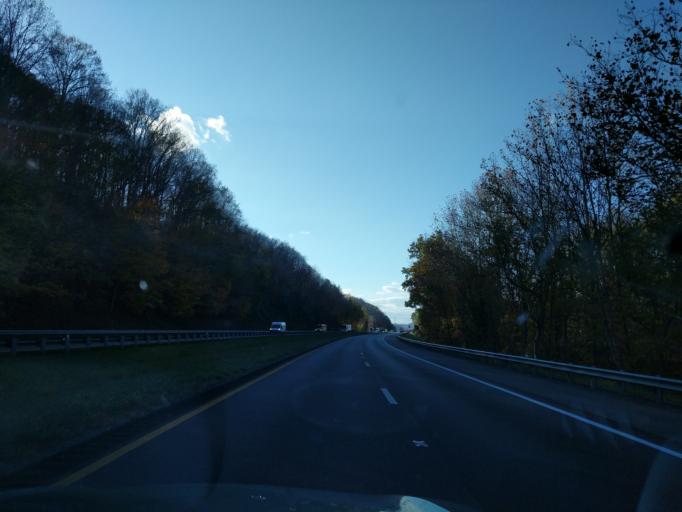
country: US
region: Virginia
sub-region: Smyth County
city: Adwolf
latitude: 36.8064
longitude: -81.6255
